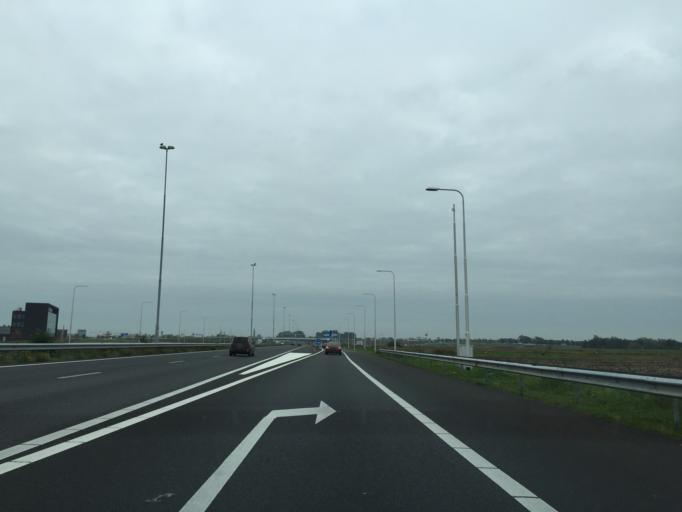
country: NL
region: North Brabant
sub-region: Gemeente Waalwijk
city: Waalwijk
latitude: 51.6923
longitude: 5.0301
